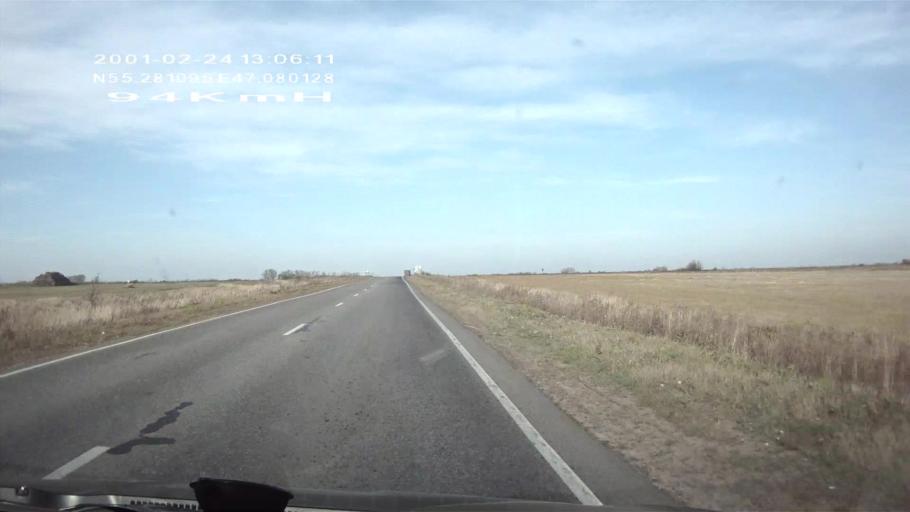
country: RU
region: Chuvashia
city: Ibresi
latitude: 55.2812
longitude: 47.0801
